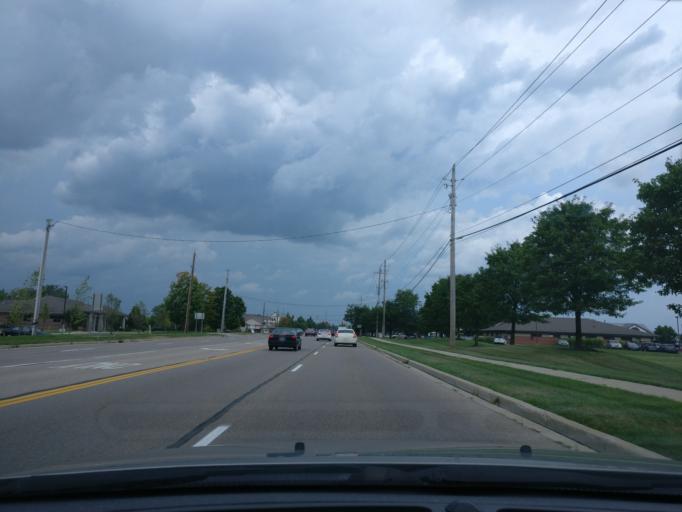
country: US
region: Ohio
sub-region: Montgomery County
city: Centerville
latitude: 39.6241
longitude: -84.1996
